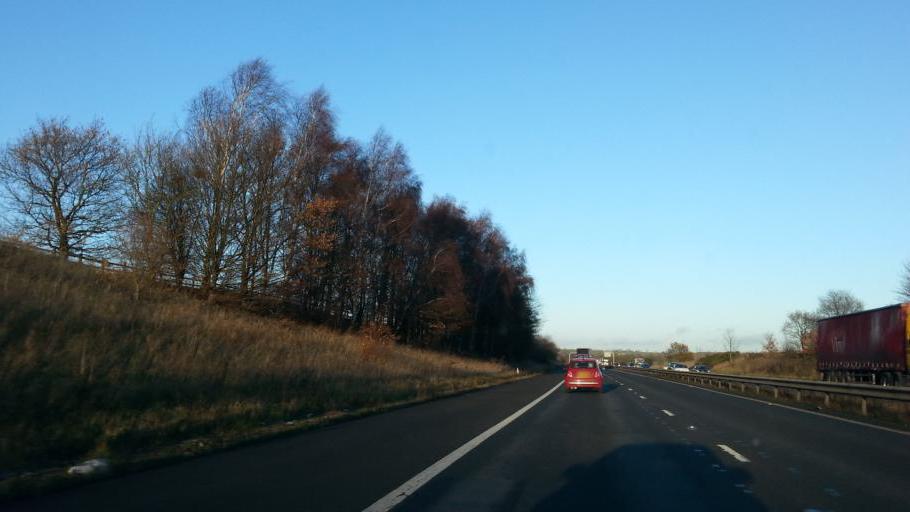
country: GB
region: England
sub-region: Derbyshire
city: Netherseal
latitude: 52.6416
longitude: -1.5998
